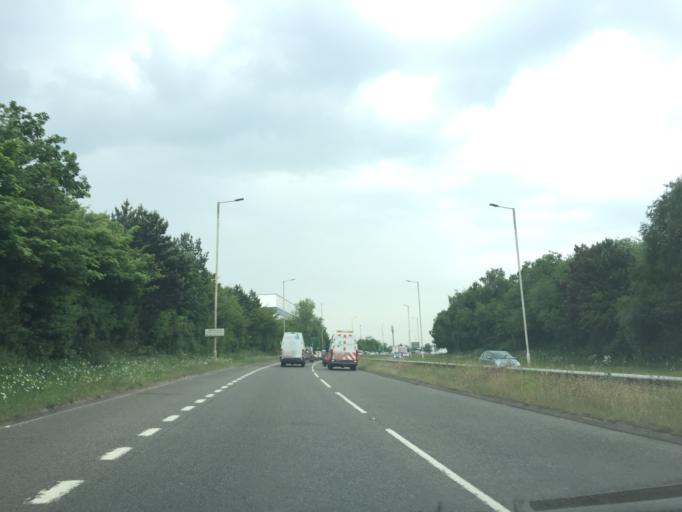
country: GB
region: England
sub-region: Poole
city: Canford Heath
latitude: 50.7421
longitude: -1.9567
